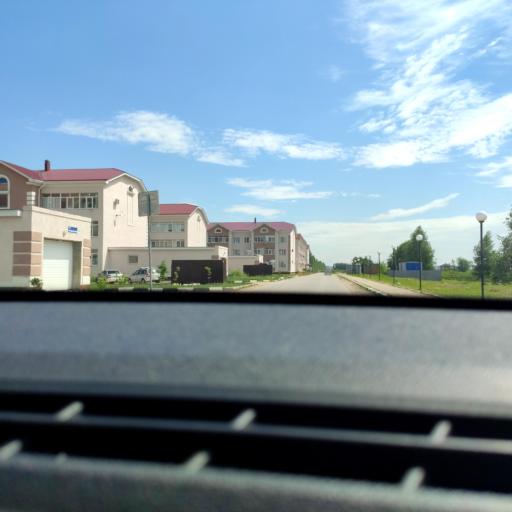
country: RU
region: Samara
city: Podstepki
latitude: 53.5274
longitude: 49.1810
